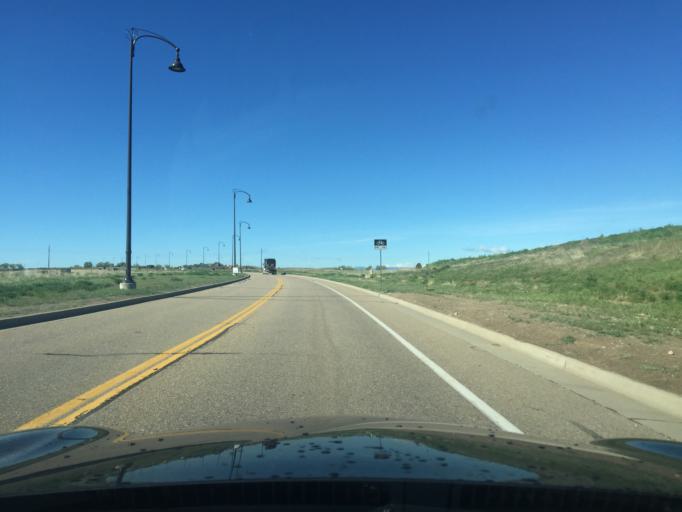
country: US
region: Colorado
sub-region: Boulder County
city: Erie
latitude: 39.9910
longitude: -105.0159
